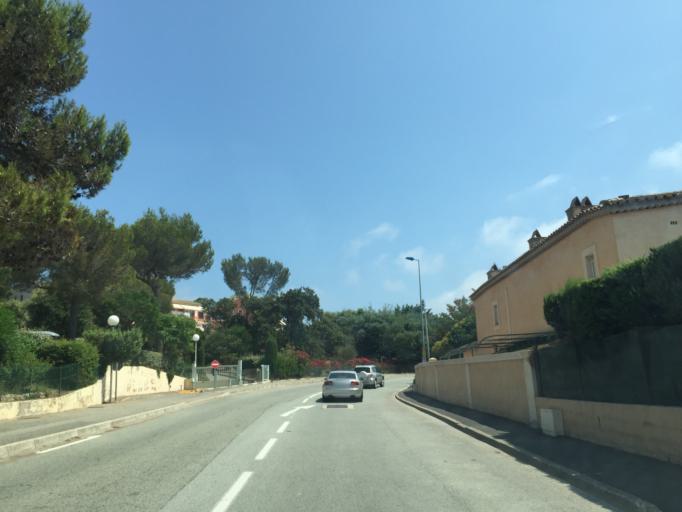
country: FR
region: Provence-Alpes-Cote d'Azur
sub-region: Departement du Var
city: Saint-Raphael
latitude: 43.4332
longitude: 6.8686
